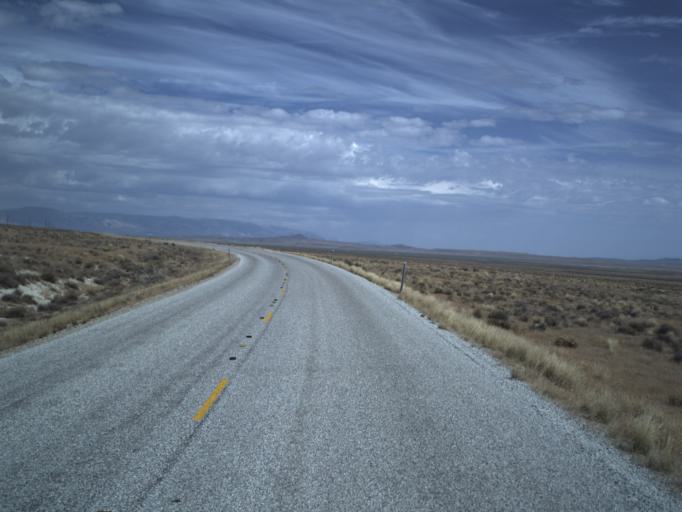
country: US
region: Utah
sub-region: Tooele County
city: Wendover
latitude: 41.5046
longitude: -113.6035
